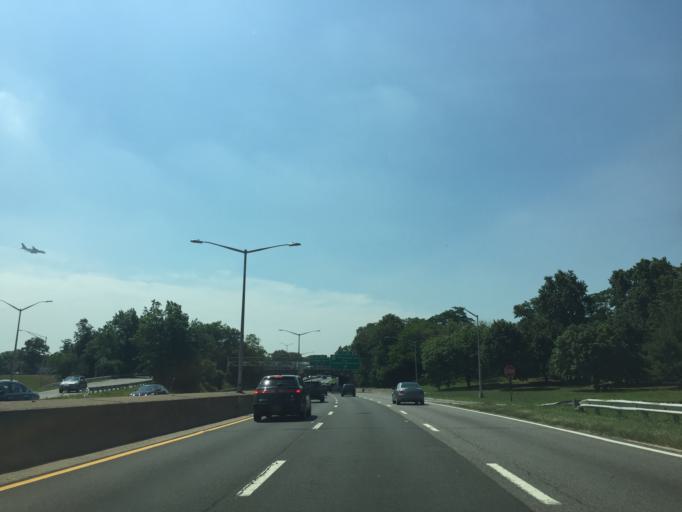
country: US
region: New York
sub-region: Nassau County
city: Bellerose Terrace
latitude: 40.7129
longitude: -73.7290
